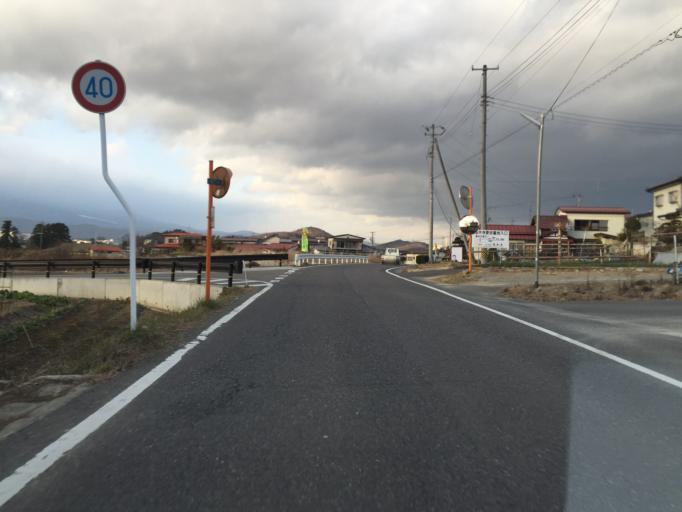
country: JP
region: Fukushima
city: Motomiya
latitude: 37.5096
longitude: 140.4112
